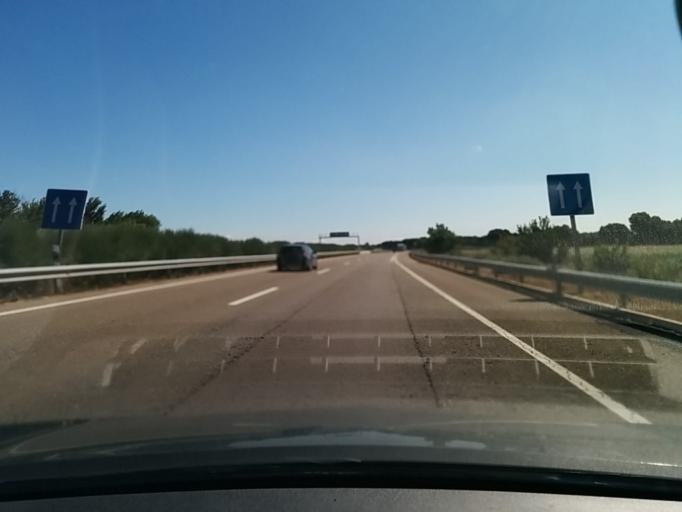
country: ES
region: Aragon
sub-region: Provincia de Huesca
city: Alcala de Gurrea
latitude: 41.9957
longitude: -0.6603
